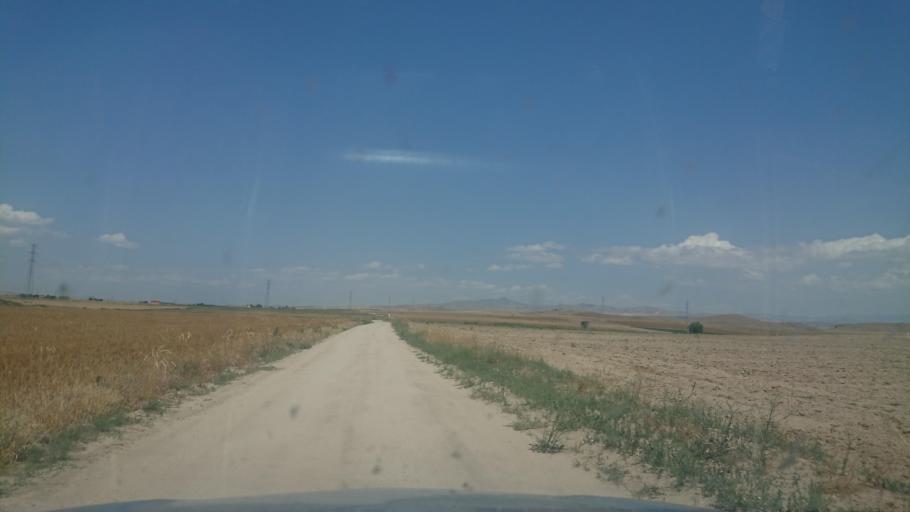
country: TR
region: Aksaray
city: Sariyahsi
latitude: 39.0056
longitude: 33.8850
